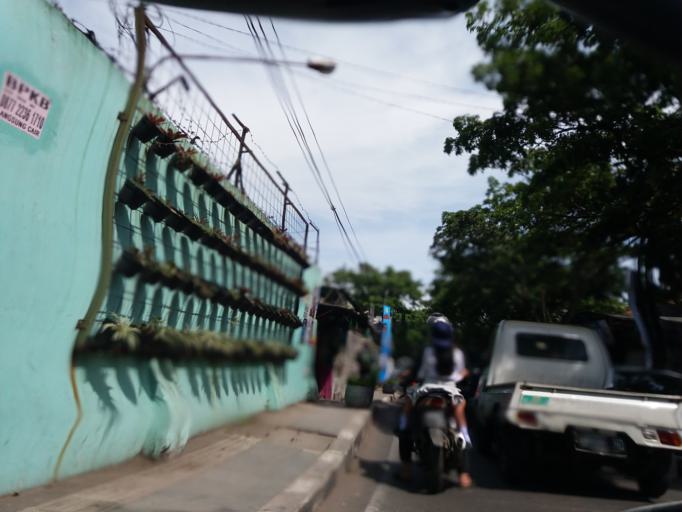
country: ID
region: West Java
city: Margahayukencana
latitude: -6.9274
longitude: 107.5743
